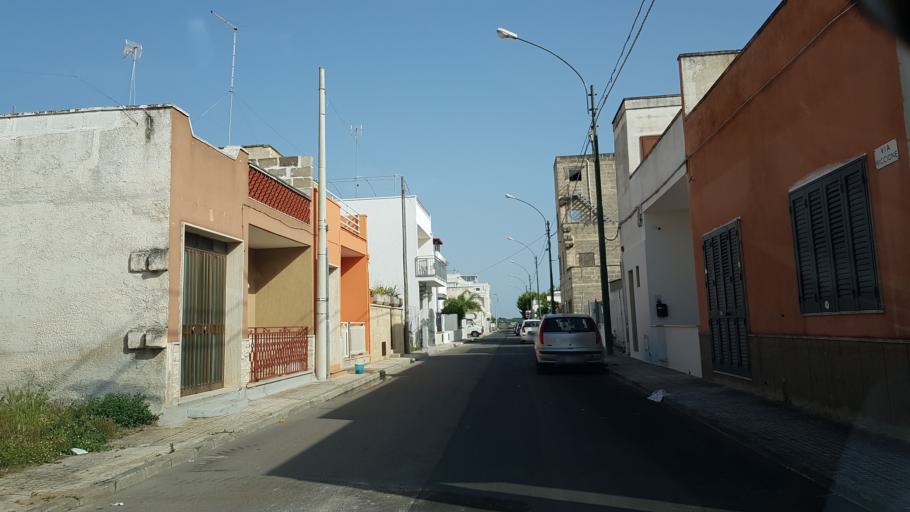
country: IT
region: Apulia
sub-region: Provincia di Lecce
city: Porto Cesareo
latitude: 40.2595
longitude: 17.9017
